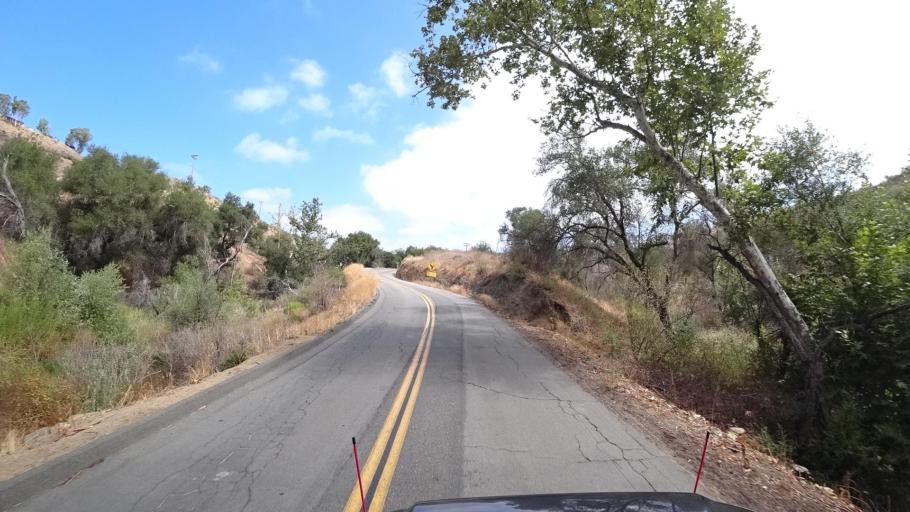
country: US
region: California
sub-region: San Diego County
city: Fallbrook
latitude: 33.4171
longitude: -117.2362
